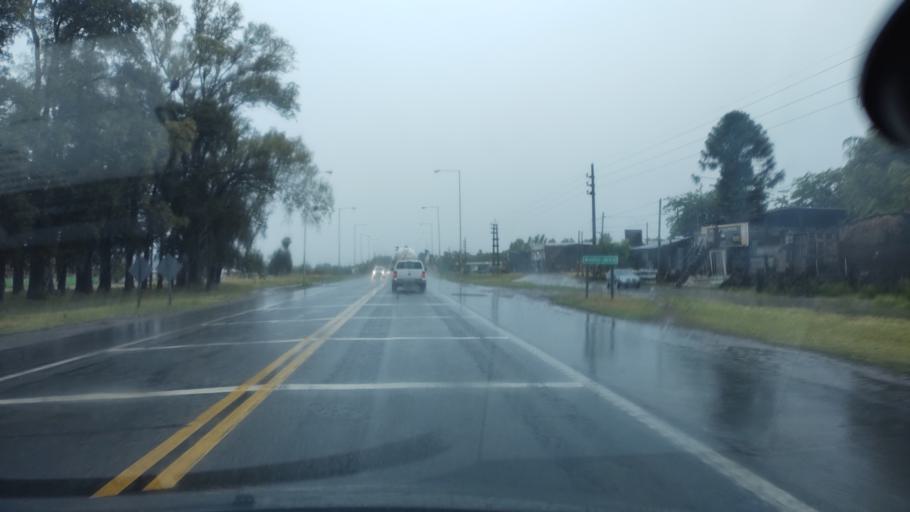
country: AR
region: Buenos Aires
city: Canuelas
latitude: -35.0438
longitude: -58.7649
